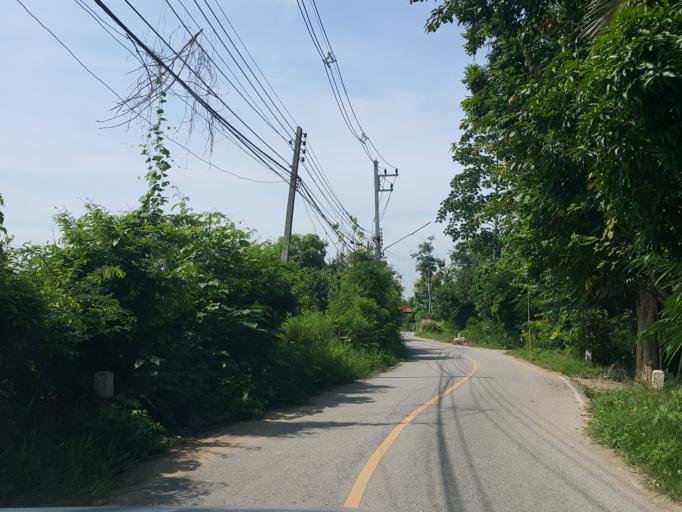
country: TH
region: Chiang Mai
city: Saraphi
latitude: 18.6964
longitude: 99.0764
